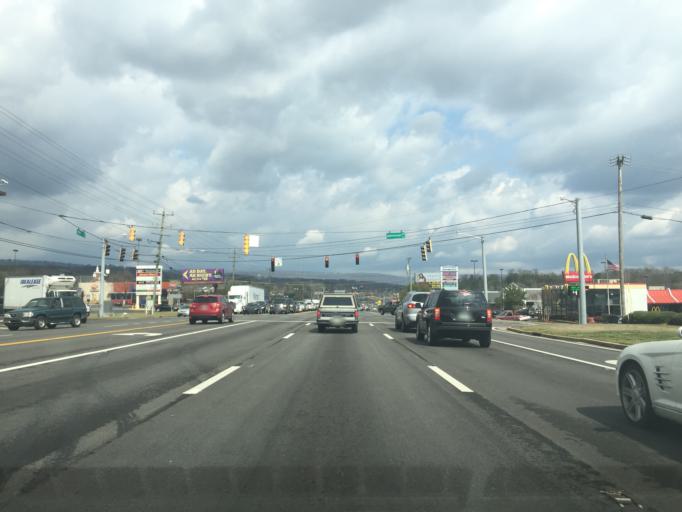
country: US
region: Tennessee
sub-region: Hamilton County
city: Red Bank
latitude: 35.1379
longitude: -85.2475
